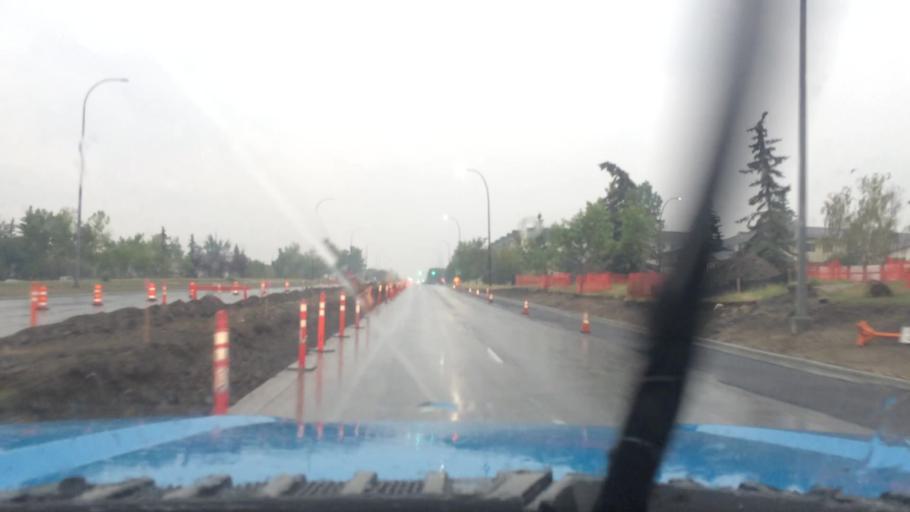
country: CA
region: Alberta
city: Calgary
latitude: 51.0946
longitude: -113.9585
